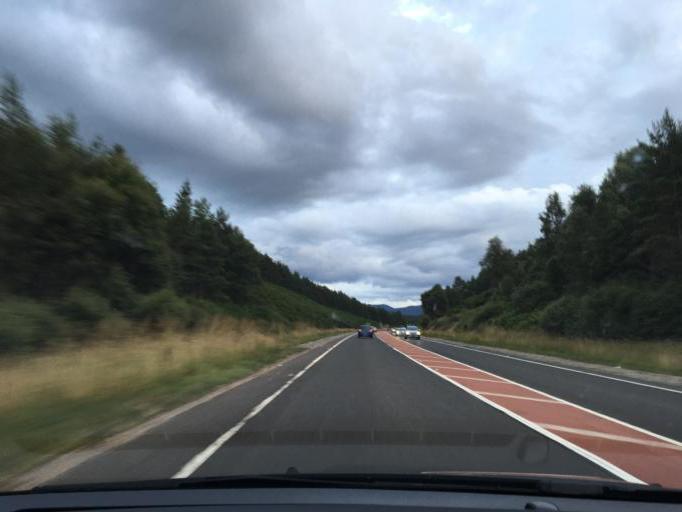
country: GB
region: Scotland
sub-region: Highland
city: Aviemore
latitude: 57.2784
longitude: -3.8281
